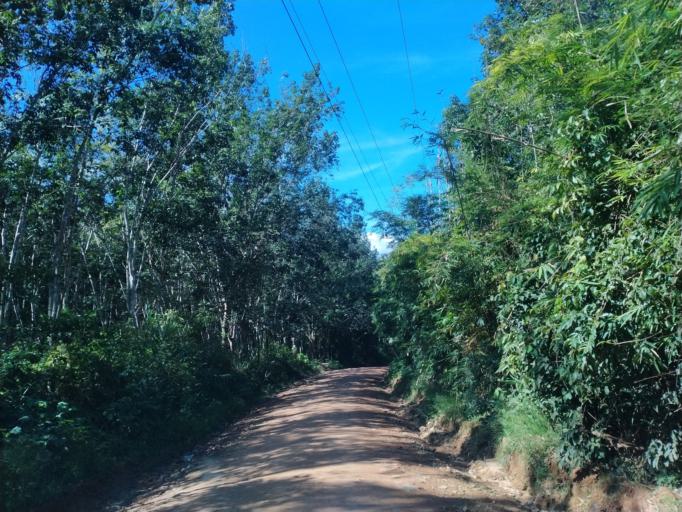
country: TH
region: Changwat Bueng Kan
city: Pak Khat
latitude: 18.6347
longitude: 103.0558
